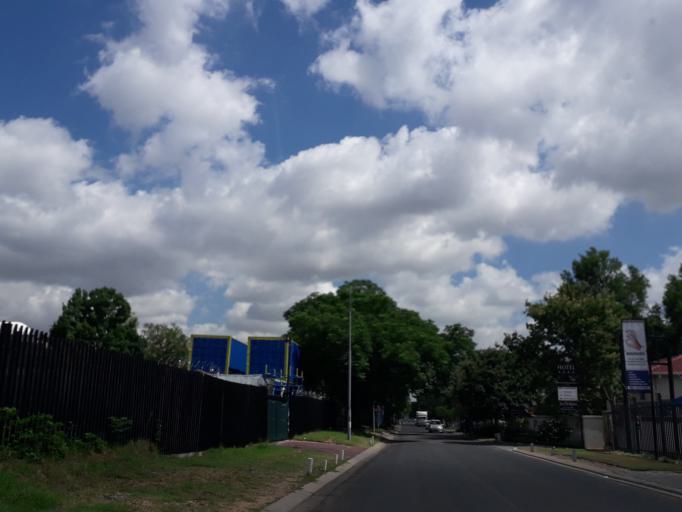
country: ZA
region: Gauteng
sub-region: City of Johannesburg Metropolitan Municipality
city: Midrand
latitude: -26.0536
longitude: 28.0616
